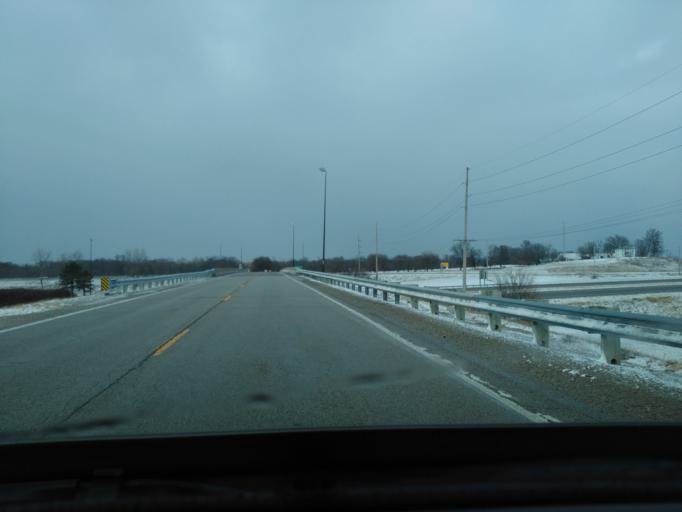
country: US
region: Illinois
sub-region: Bond County
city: Greenville
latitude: 38.8526
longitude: -89.4512
